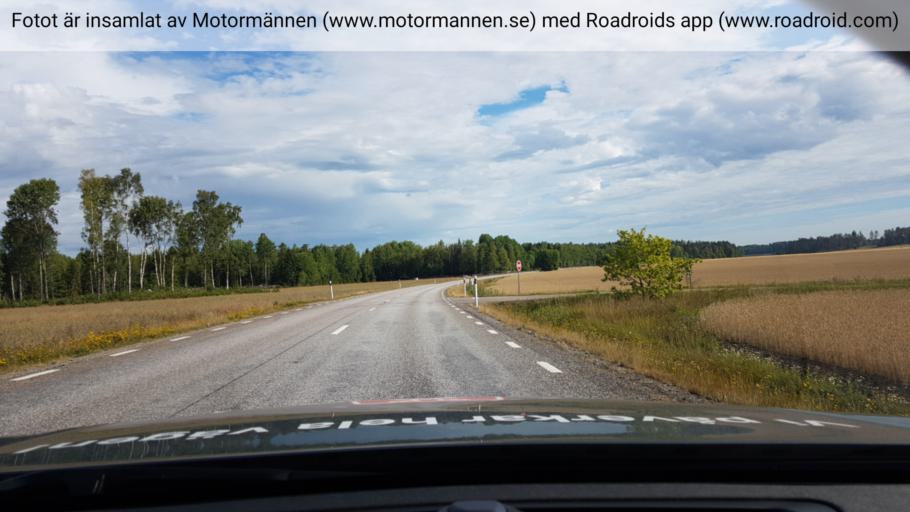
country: SE
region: Uppsala
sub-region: Enkopings Kommun
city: Irsta
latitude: 59.7992
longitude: 16.9014
